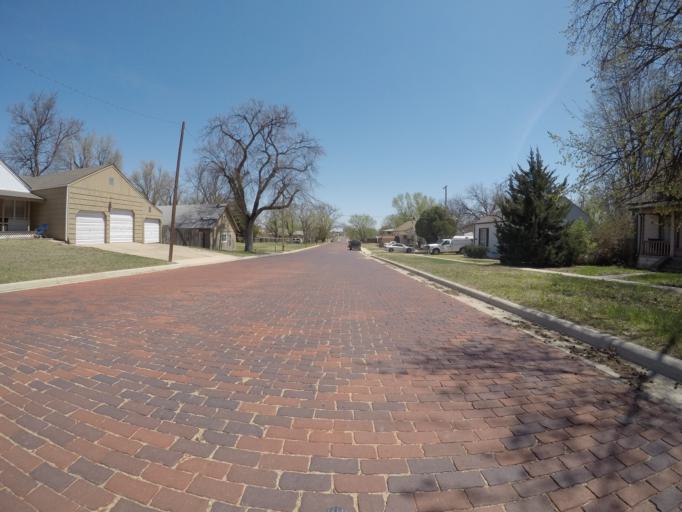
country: US
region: Kansas
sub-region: Pratt County
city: Pratt
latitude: 37.6419
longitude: -98.7472
